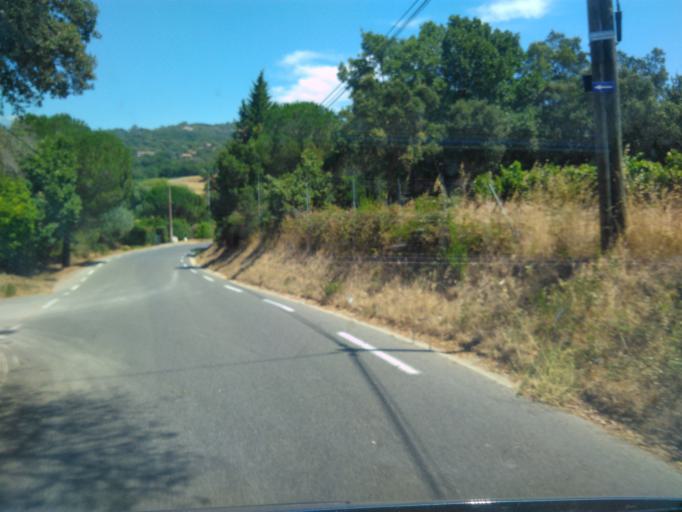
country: FR
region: Provence-Alpes-Cote d'Azur
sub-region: Departement du Var
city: La Croix-Valmer
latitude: 43.2131
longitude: 6.5783
